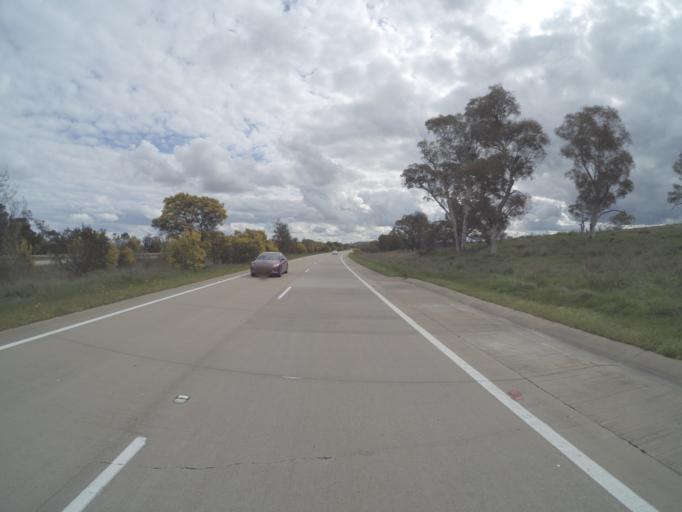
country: AU
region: New South Wales
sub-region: Goulburn Mulwaree
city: Goulburn
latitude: -34.8113
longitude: 149.4800
